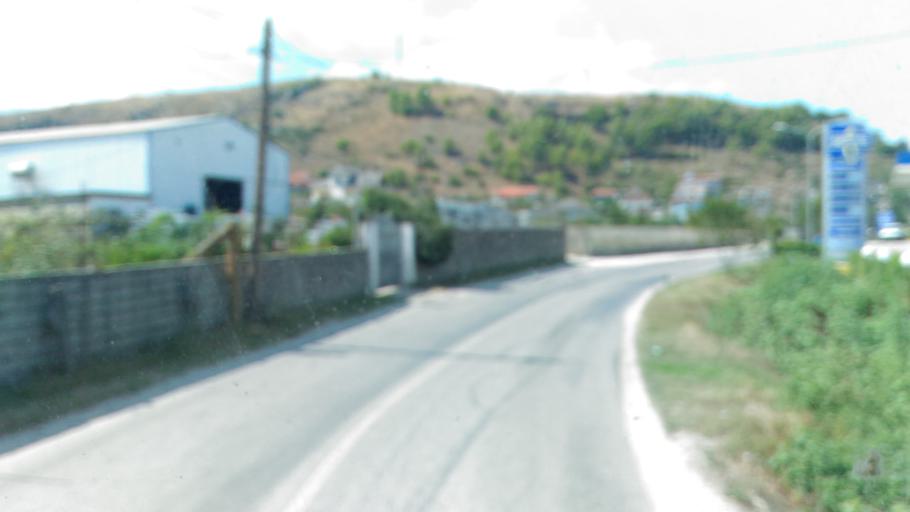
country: AL
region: Gjirokaster
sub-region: Rrethi i Gjirokastres
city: Dervician
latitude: 40.0569
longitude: 20.1732
